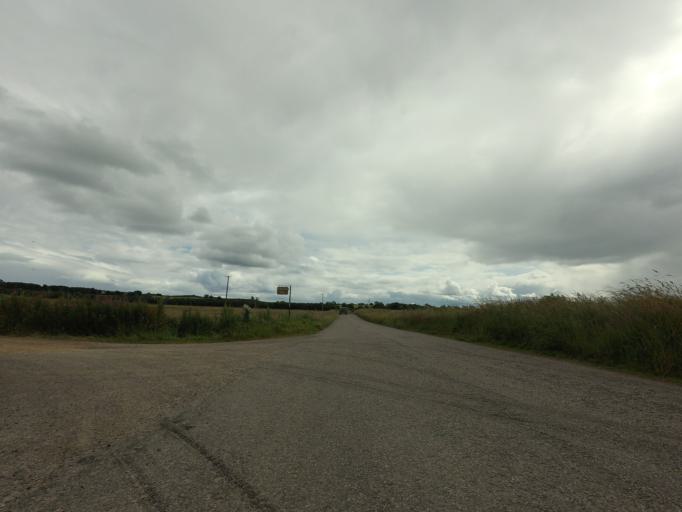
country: GB
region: Scotland
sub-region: Moray
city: Lhanbryd
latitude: 57.6576
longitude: -3.2092
